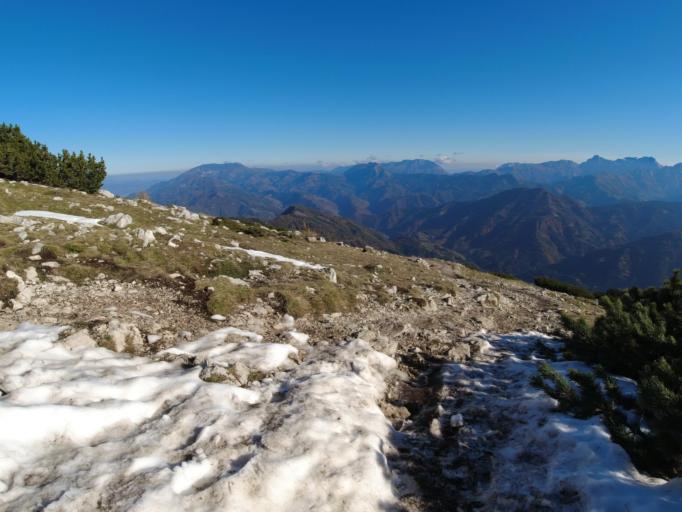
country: AT
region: Carinthia
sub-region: Politischer Bezirk Volkermarkt
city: Gallizien
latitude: 46.5013
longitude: 14.4907
